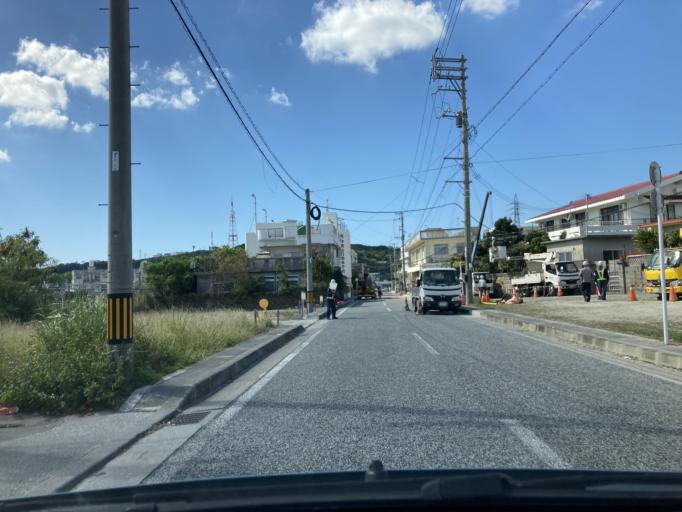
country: JP
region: Okinawa
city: Tomigusuku
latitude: 26.1876
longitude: 127.7128
